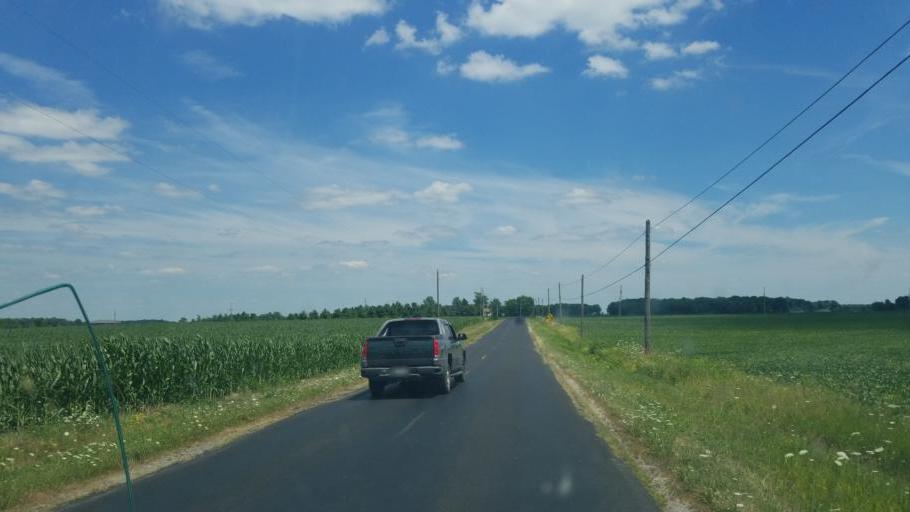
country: US
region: Ohio
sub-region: Williams County
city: Edgerton
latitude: 41.4663
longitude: -84.6949
